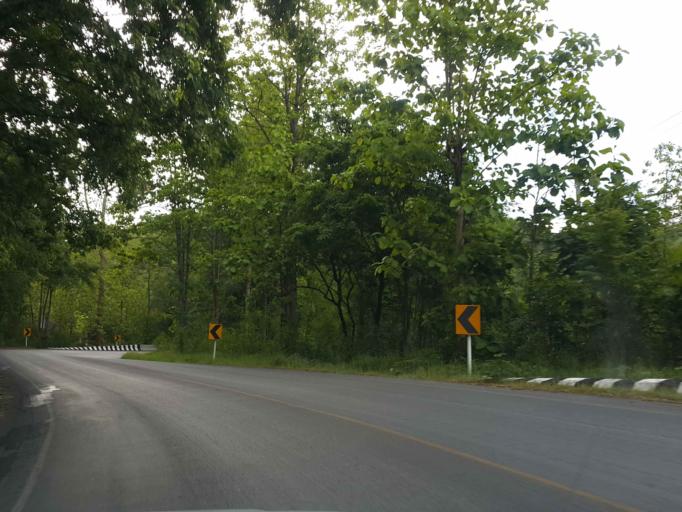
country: TH
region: Lampang
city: Thoen
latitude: 17.6171
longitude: 99.3212
